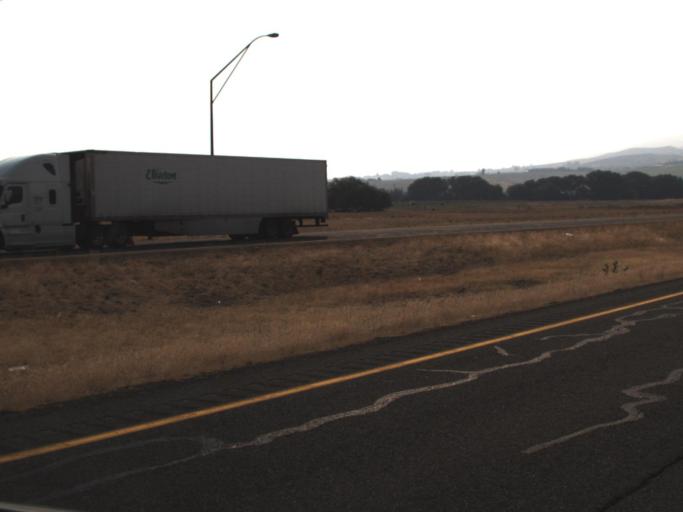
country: US
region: Washington
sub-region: Kittitas County
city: Ellensburg
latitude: 46.9330
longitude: -120.5043
